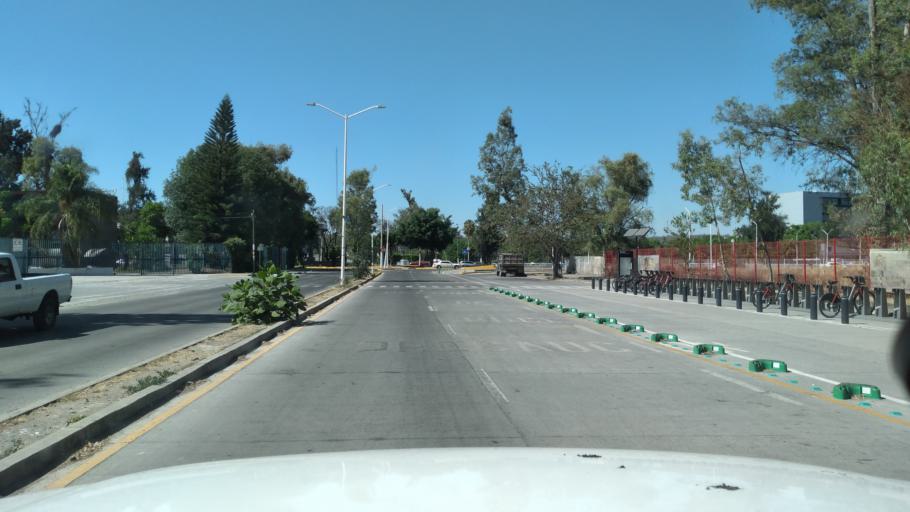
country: MX
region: Jalisco
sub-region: Zapopan
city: Zapopan
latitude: 20.7381
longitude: -103.3832
